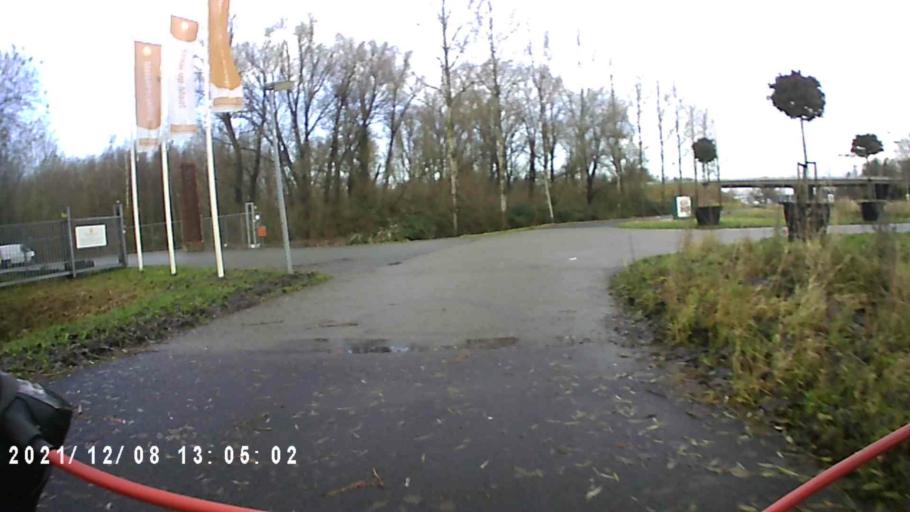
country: NL
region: Groningen
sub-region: Gemeente Haren
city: Haren
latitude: 53.2025
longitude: 6.6146
